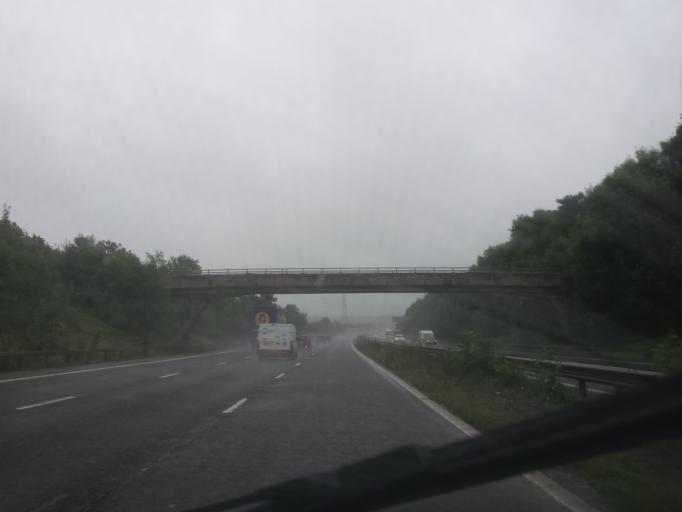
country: GB
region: England
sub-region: Leicestershire
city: Kirby Muxloe
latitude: 52.6504
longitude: -1.2353
